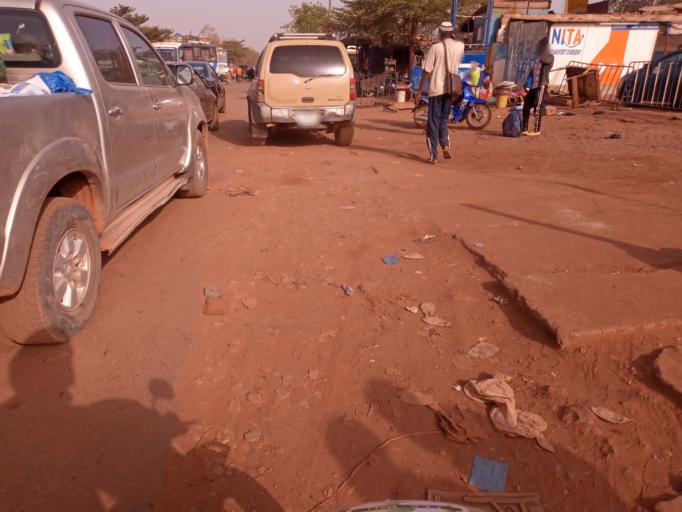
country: ML
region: Bamako
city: Bamako
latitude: 12.5973
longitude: -7.9595
